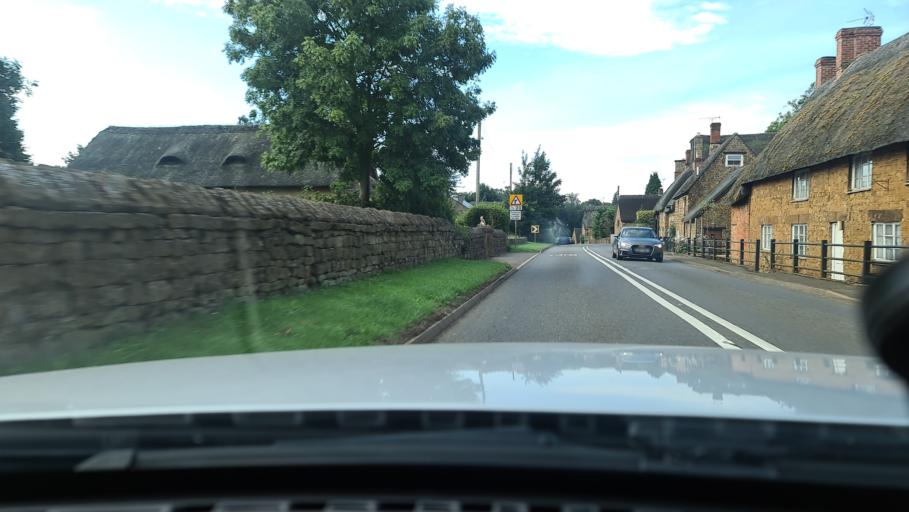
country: GB
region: England
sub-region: Oxfordshire
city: Hanwell
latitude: 52.0745
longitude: -1.3922
